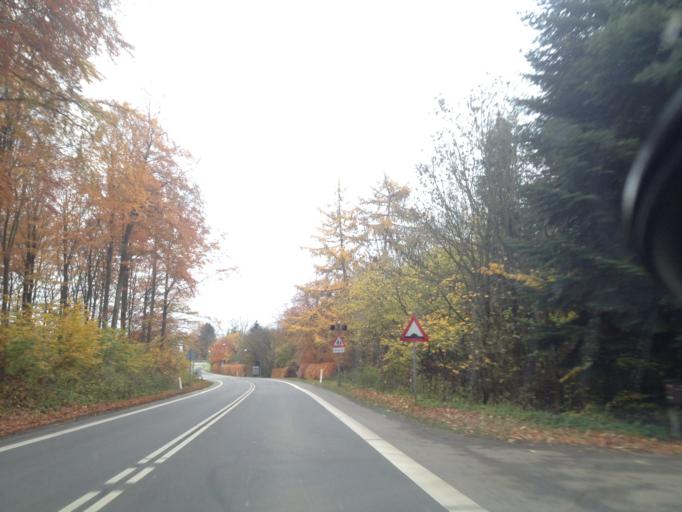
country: DK
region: South Denmark
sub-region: Nordfyns Kommune
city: Sonderso
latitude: 55.4431
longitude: 10.1995
